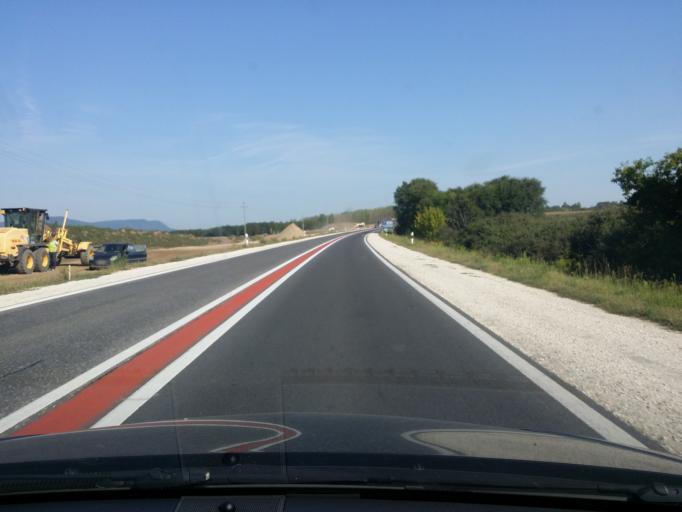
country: HU
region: Pest
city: Dunakeszi
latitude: 47.6469
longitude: 19.1615
